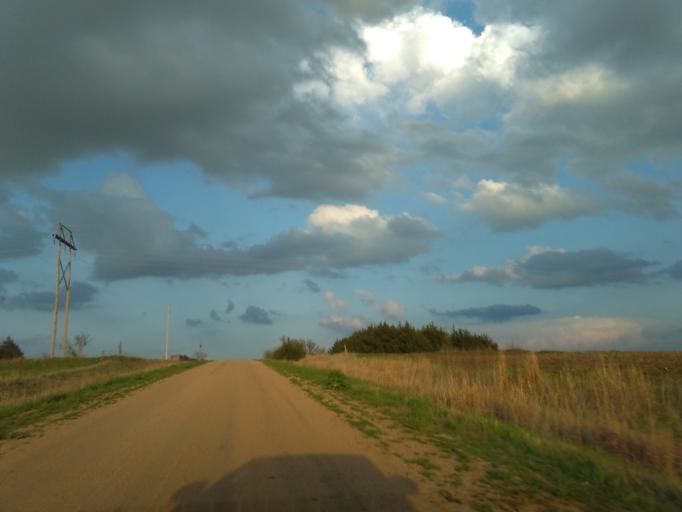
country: US
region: Nebraska
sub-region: Webster County
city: Red Cloud
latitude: 40.2199
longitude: -98.3408
